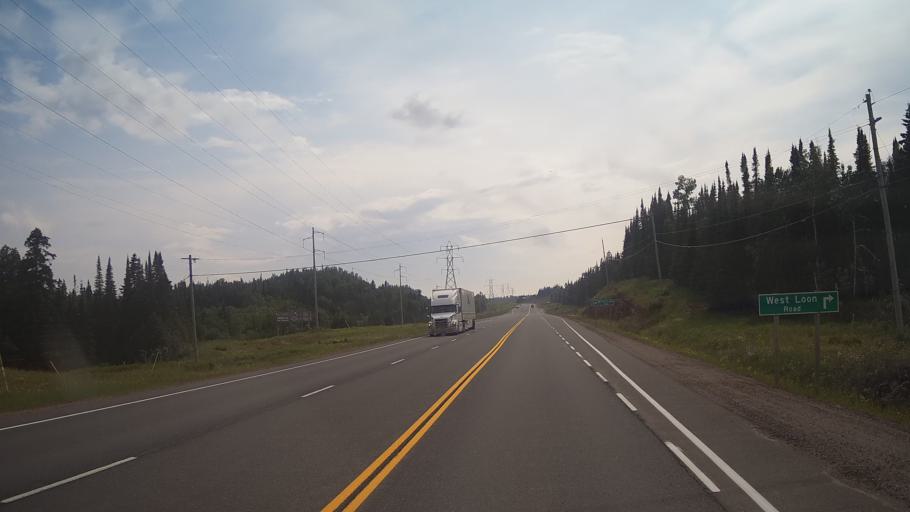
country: CA
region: Ontario
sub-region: Thunder Bay District
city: Thunder Bay
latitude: 48.6278
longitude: -88.7540
